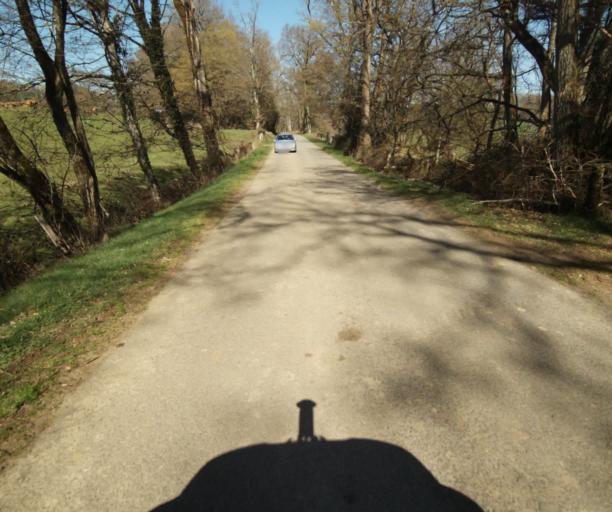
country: FR
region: Limousin
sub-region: Departement de la Correze
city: Saint-Clement
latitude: 45.2970
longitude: 1.7061
